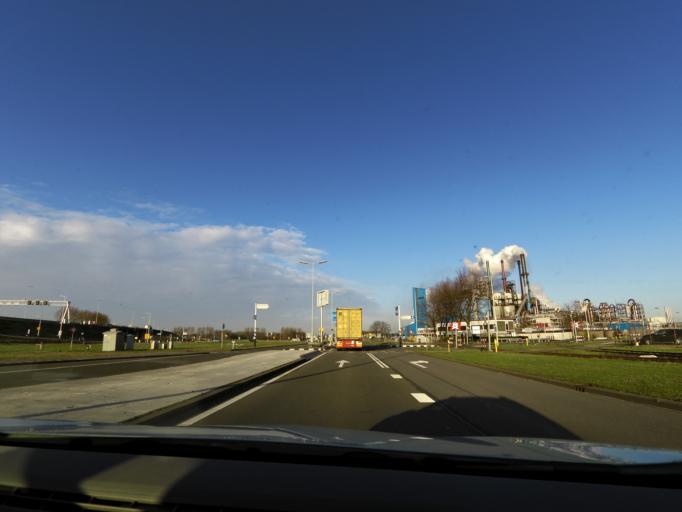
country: NL
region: South Holland
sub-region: Gemeente Maassluis
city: Maassluis
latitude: 51.8897
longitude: 4.2613
